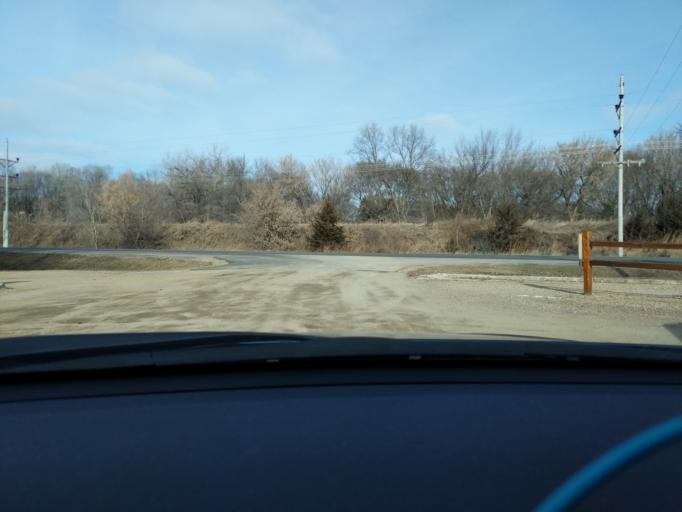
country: US
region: Minnesota
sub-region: Chippewa County
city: Montevideo
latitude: 44.9189
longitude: -95.6979
